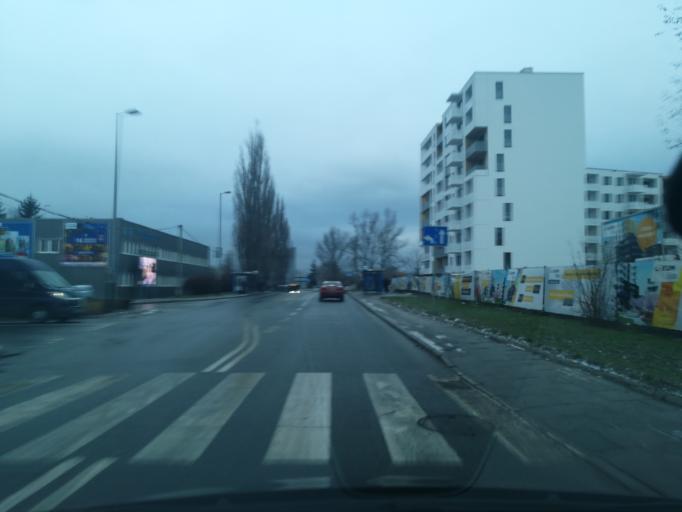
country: PL
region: Lesser Poland Voivodeship
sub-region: Krakow
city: Krakow
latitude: 50.0235
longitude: 19.9604
